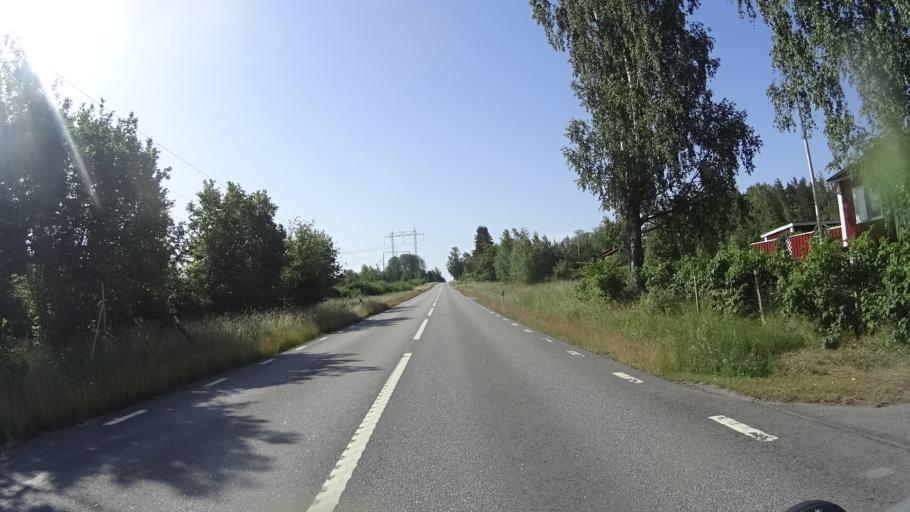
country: SE
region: OEstergoetland
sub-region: Atvidabergs Kommun
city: Atvidaberg
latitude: 58.1548
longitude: 16.0701
